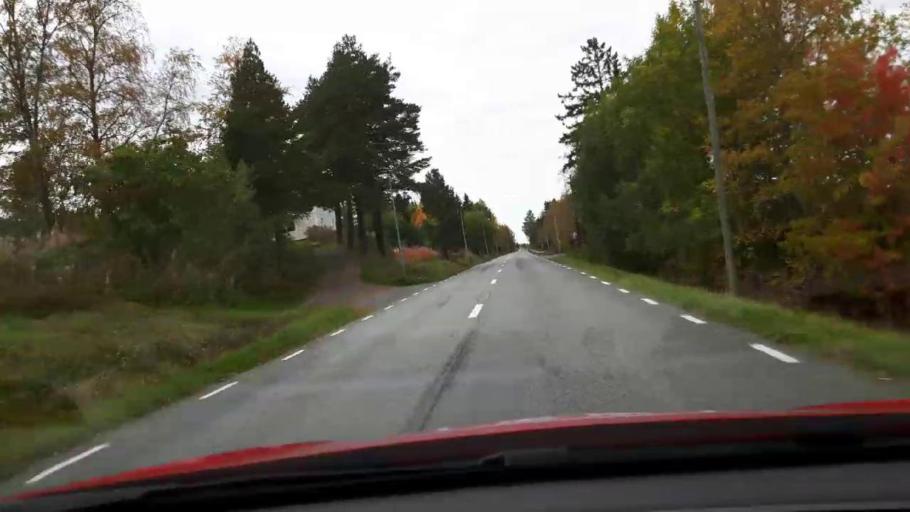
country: SE
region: Jaemtland
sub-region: Krokoms Kommun
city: Krokom
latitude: 63.1824
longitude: 14.0809
